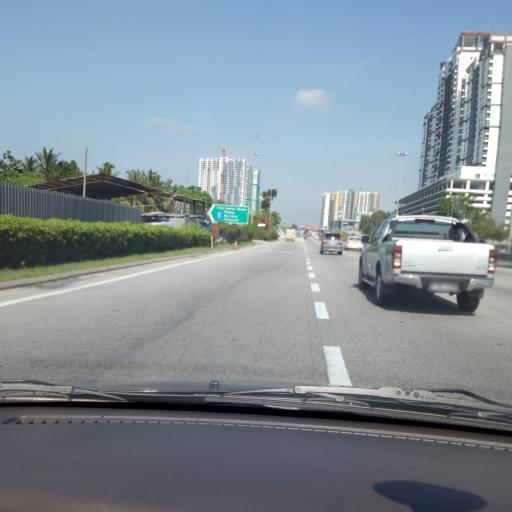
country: MY
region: Selangor
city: Kampong Baharu Balakong
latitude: 3.0297
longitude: 101.7610
